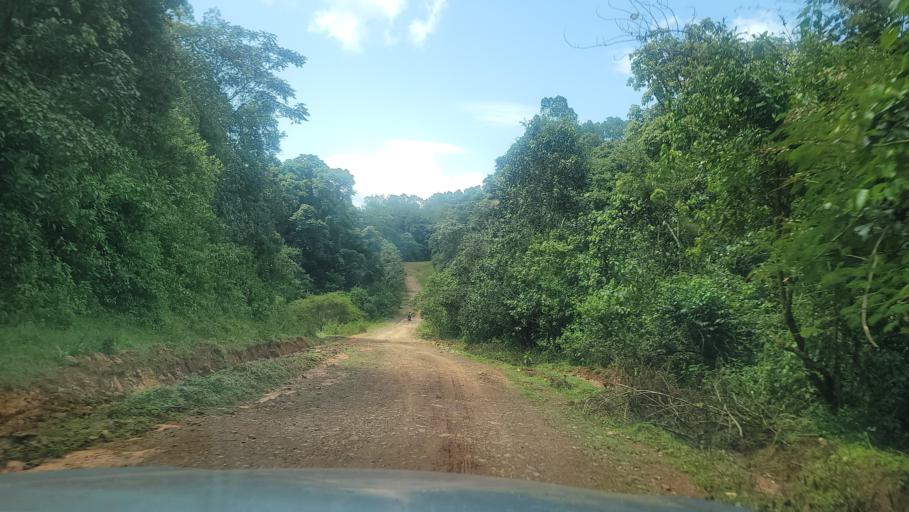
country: ET
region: Southern Nations, Nationalities, and People's Region
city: Bonga
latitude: 7.6778
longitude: 36.2418
